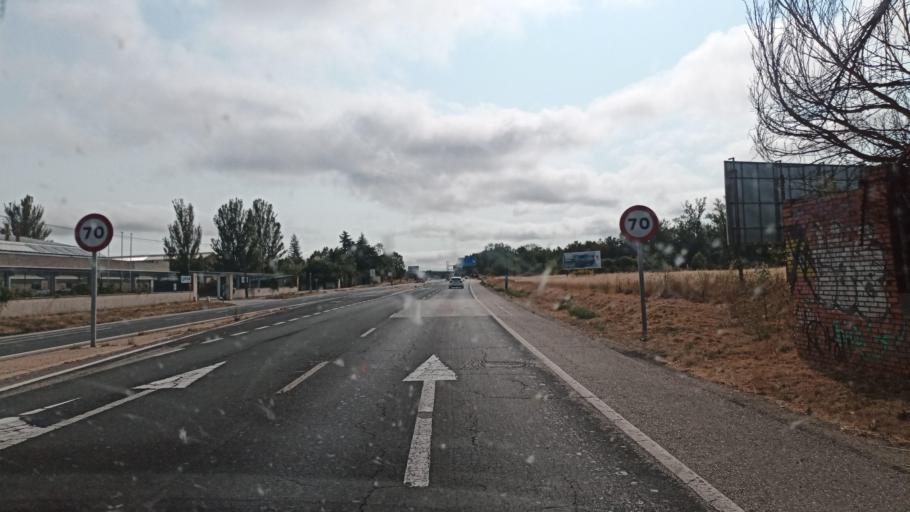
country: ES
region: Castille and Leon
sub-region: Provincia de Burgos
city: Burgos
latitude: 42.3447
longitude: -3.6467
